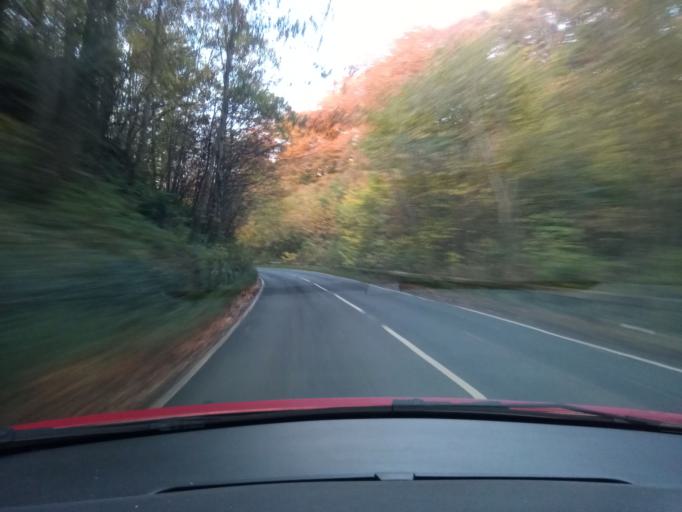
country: GB
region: England
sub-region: Northumberland
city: Bardon Mill
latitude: 54.9630
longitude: -2.2448
